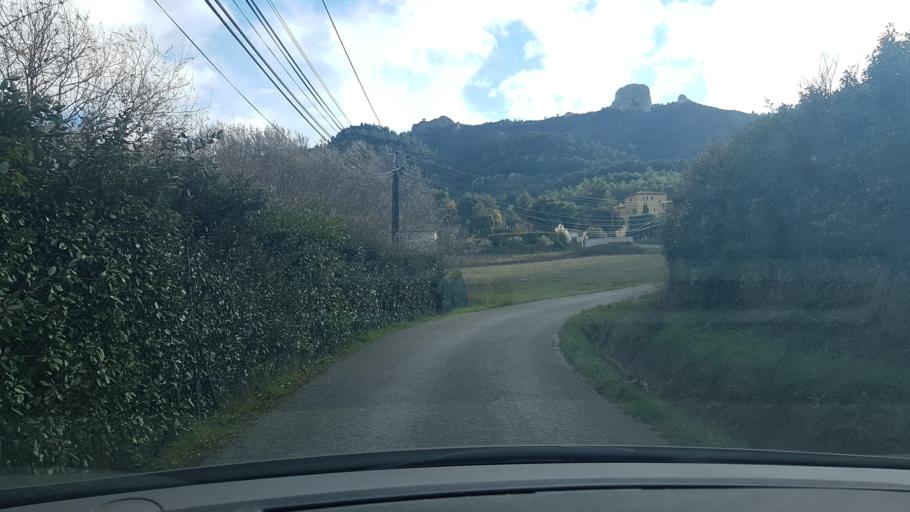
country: FR
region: Provence-Alpes-Cote d'Azur
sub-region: Departement des Bouches-du-Rhone
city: Simiane-Collongue
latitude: 43.4172
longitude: 5.4629
